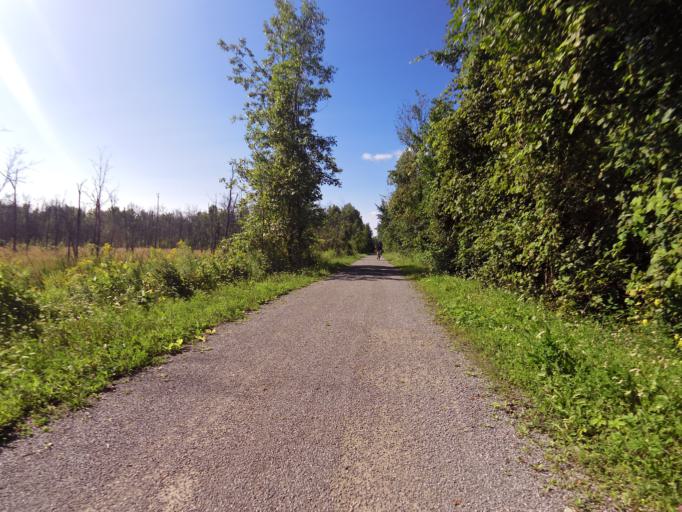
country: CA
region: Ontario
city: Ottawa
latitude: 45.2150
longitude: -75.6238
